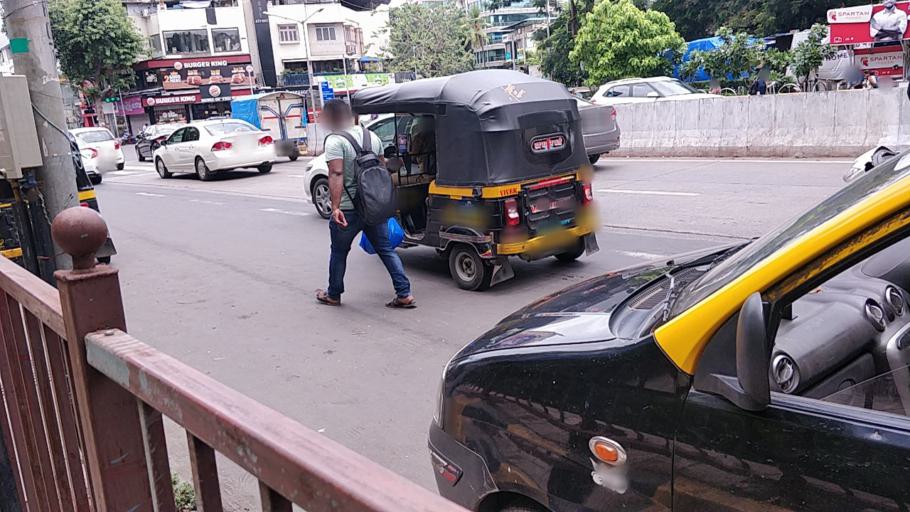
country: IN
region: Maharashtra
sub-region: Mumbai Suburban
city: Mumbai
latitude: 19.0642
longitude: 72.8350
